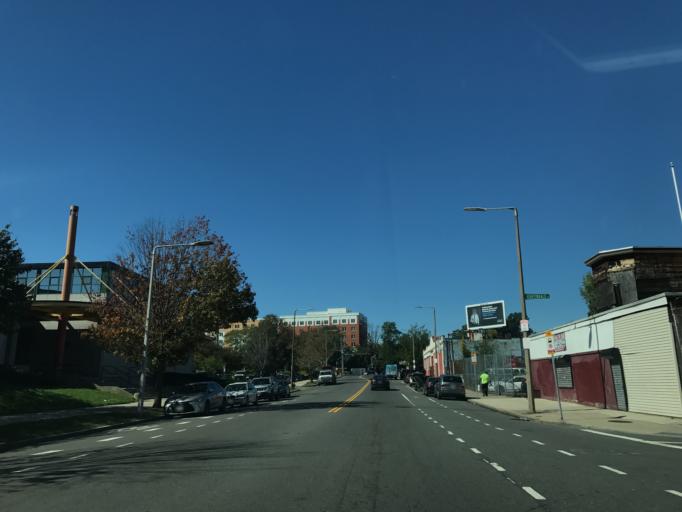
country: US
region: Massachusetts
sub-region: Suffolk County
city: Jamaica Plain
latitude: 42.2943
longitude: -71.0857
